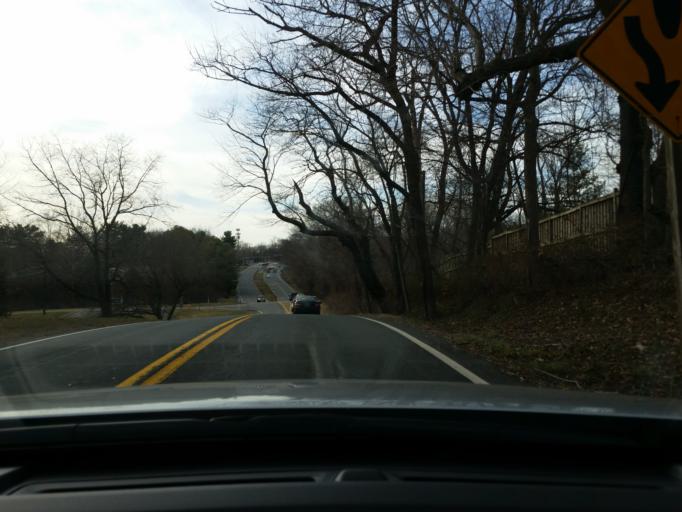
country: US
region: Virginia
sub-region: Fairfax County
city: McLean
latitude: 38.9529
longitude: -77.1864
